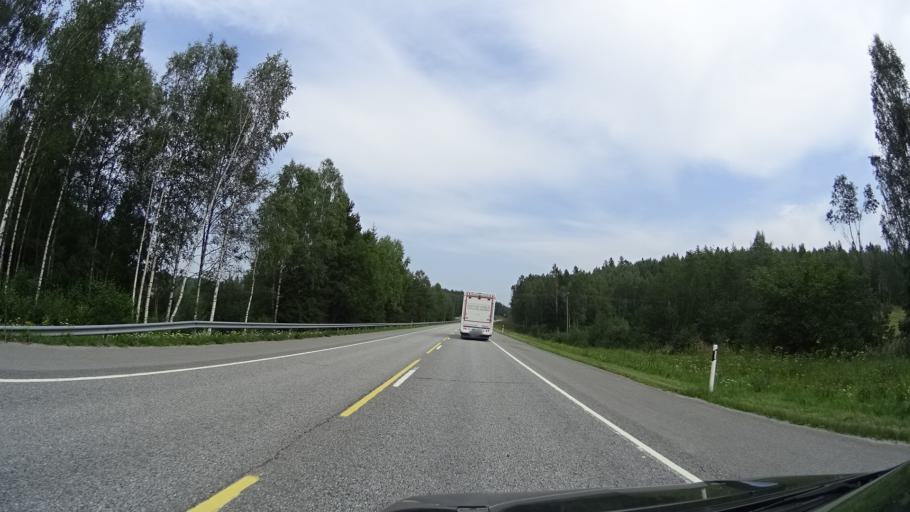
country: FI
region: Uusimaa
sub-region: Raaseporin
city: Karis
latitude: 60.0677
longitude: 23.7986
